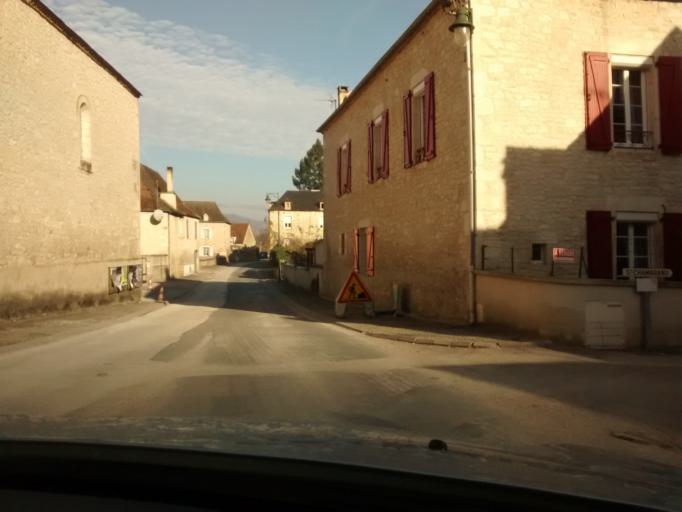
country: FR
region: Midi-Pyrenees
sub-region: Departement du Lot
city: Souillac
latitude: 44.8657
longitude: 1.4408
